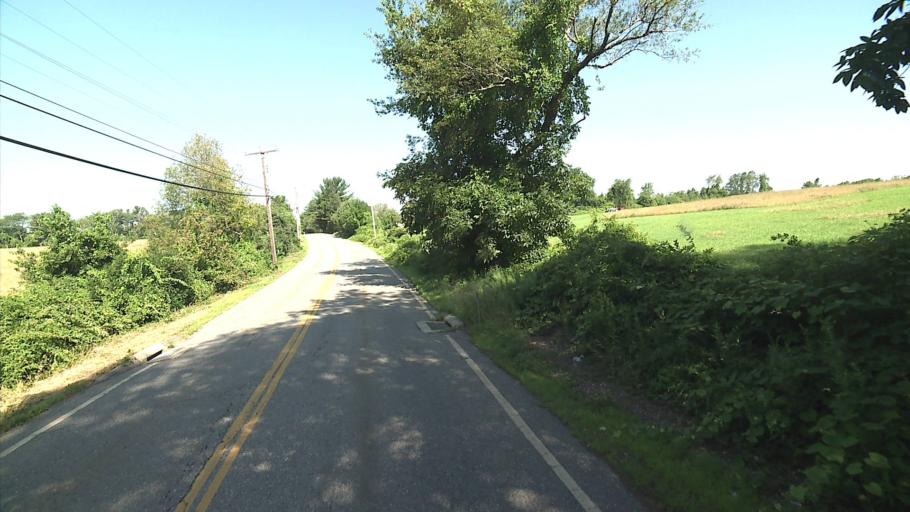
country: US
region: Connecticut
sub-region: New London County
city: Montville Center
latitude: 41.4922
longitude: -72.1767
